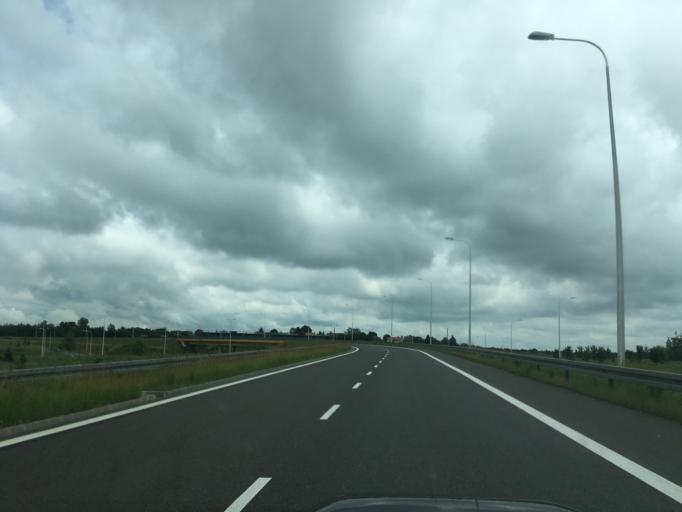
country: PL
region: Lublin Voivodeship
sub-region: Powiat lubelski
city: Jastkow
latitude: 51.2826
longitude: 22.4521
